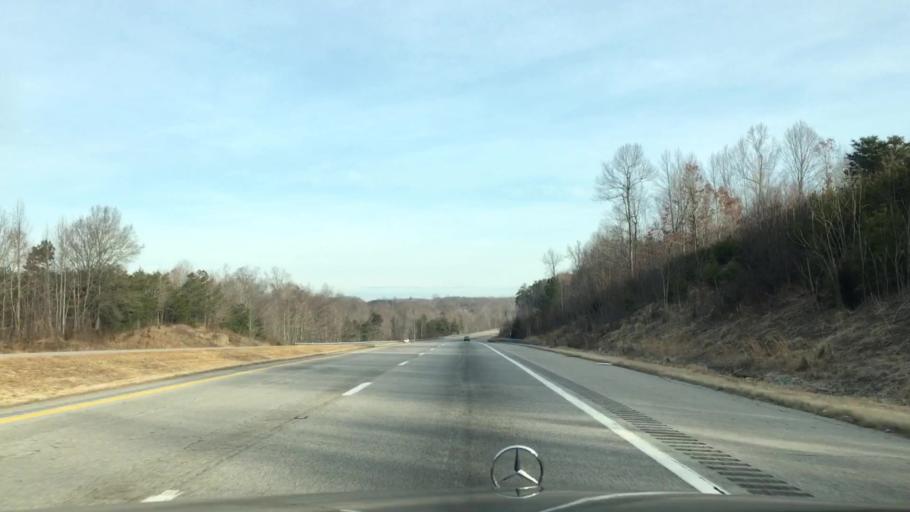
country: US
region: Virginia
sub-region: Pittsylvania County
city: Mount Hermon
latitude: 36.6624
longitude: -79.3656
